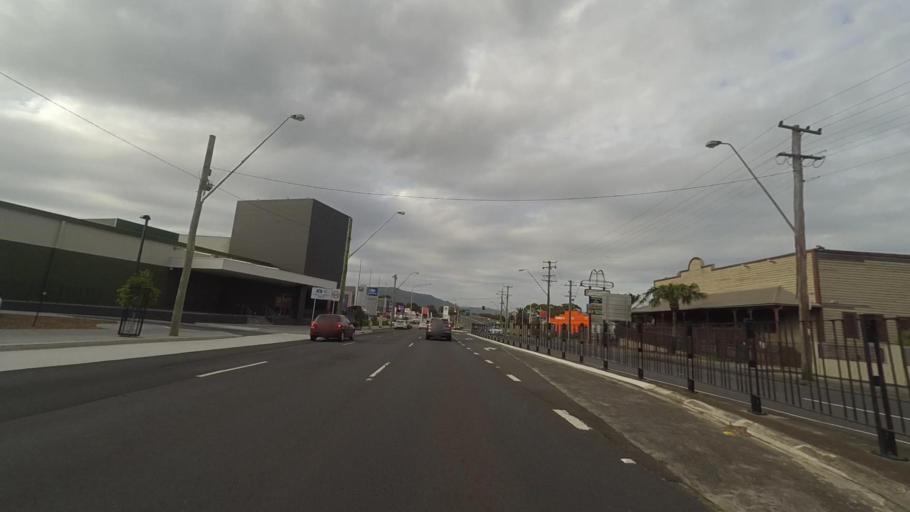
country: AU
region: New South Wales
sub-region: Wollongong
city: Gwynneville
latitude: -34.4132
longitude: 150.8927
